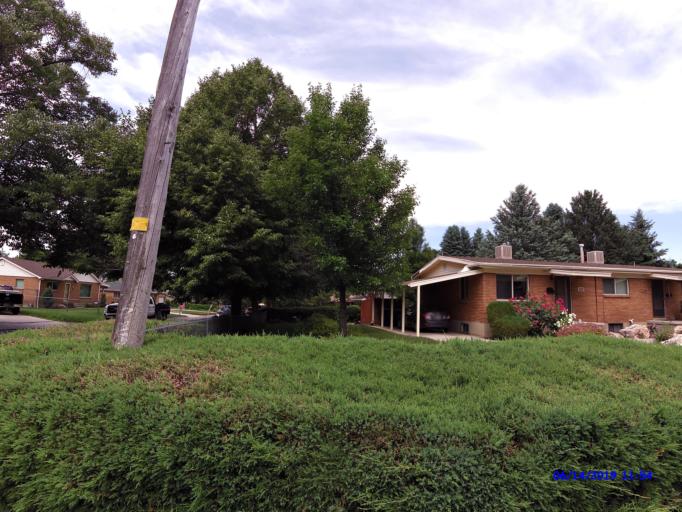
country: US
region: Utah
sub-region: Weber County
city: Ogden
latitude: 41.2569
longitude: -111.9450
